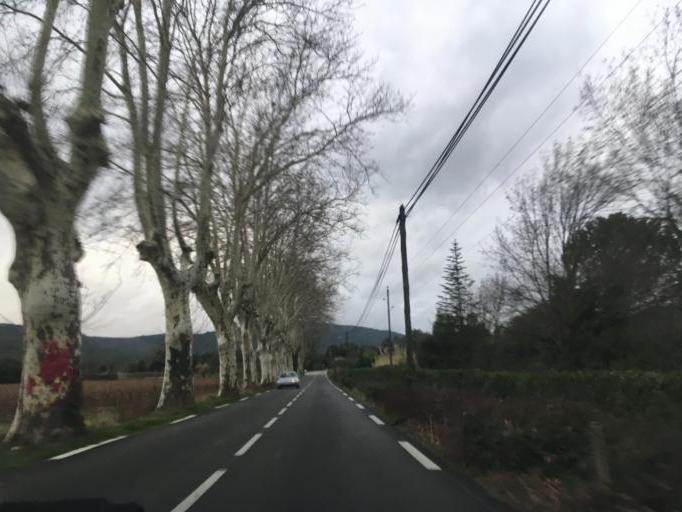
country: FR
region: Provence-Alpes-Cote d'Azur
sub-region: Departement du Var
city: Besse-sur-Issole
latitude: 43.3416
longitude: 6.1677
